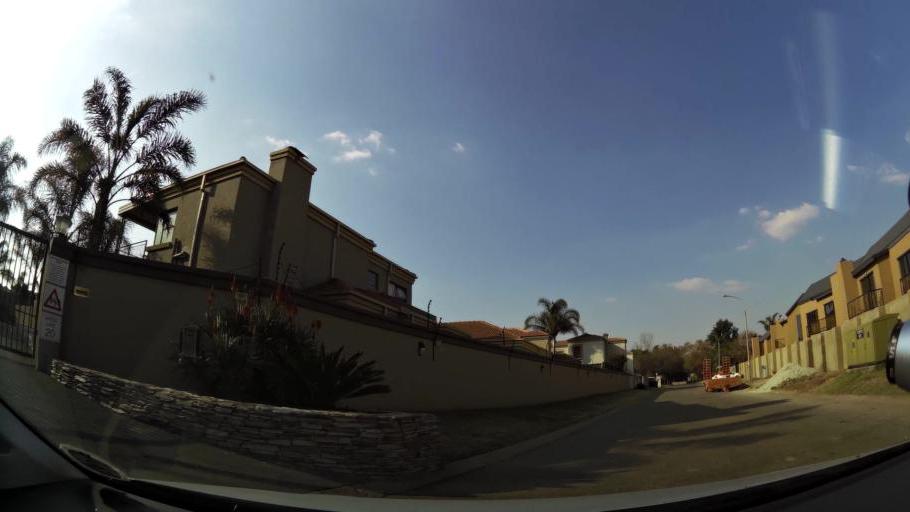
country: ZA
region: Gauteng
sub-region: City of Johannesburg Metropolitan Municipality
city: Modderfontein
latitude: -26.0816
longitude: 28.1999
